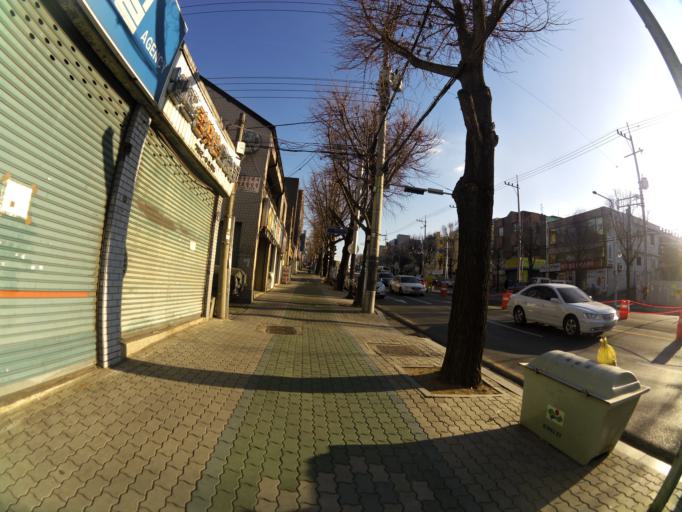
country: KR
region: Daegu
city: Daegu
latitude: 35.8767
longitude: 128.6331
